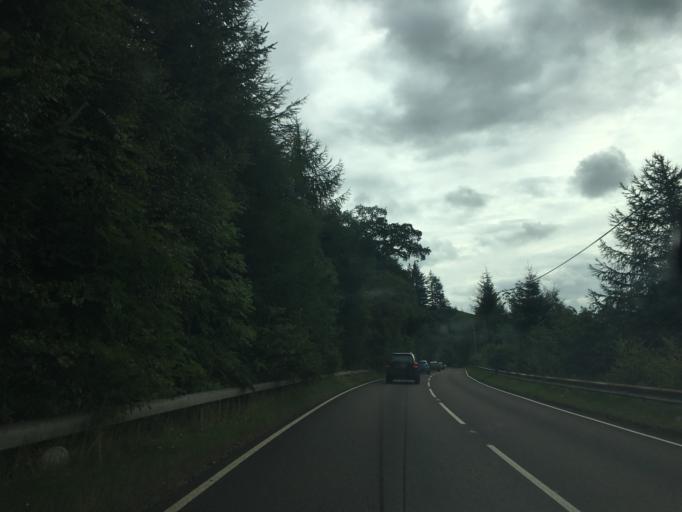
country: GB
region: Scotland
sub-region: Stirling
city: Callander
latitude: 56.2911
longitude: -4.2859
